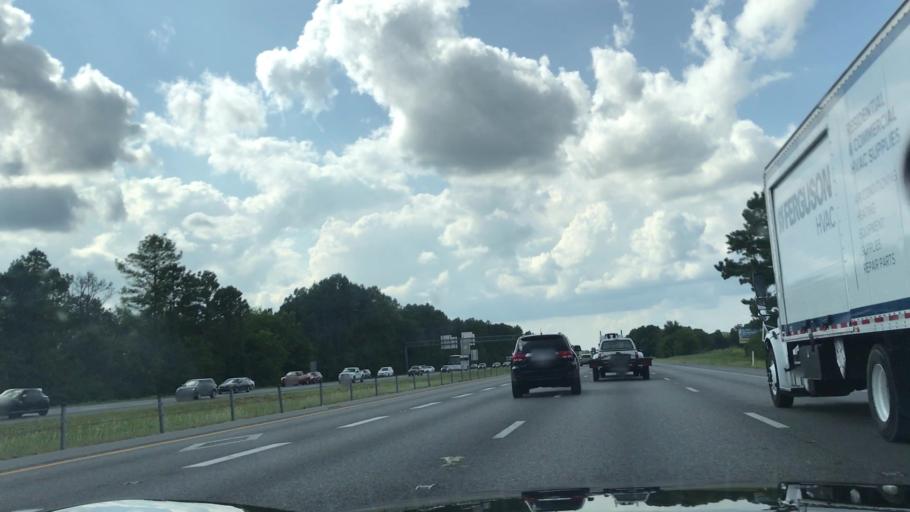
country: US
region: Tennessee
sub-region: Rutherford County
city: Smyrna
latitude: 35.8983
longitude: -86.4912
